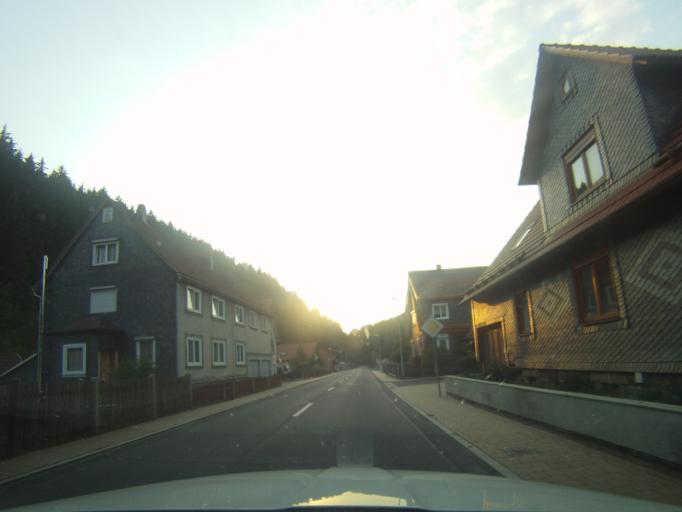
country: DE
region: Thuringia
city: Eisfeld
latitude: 50.4939
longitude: 10.8619
